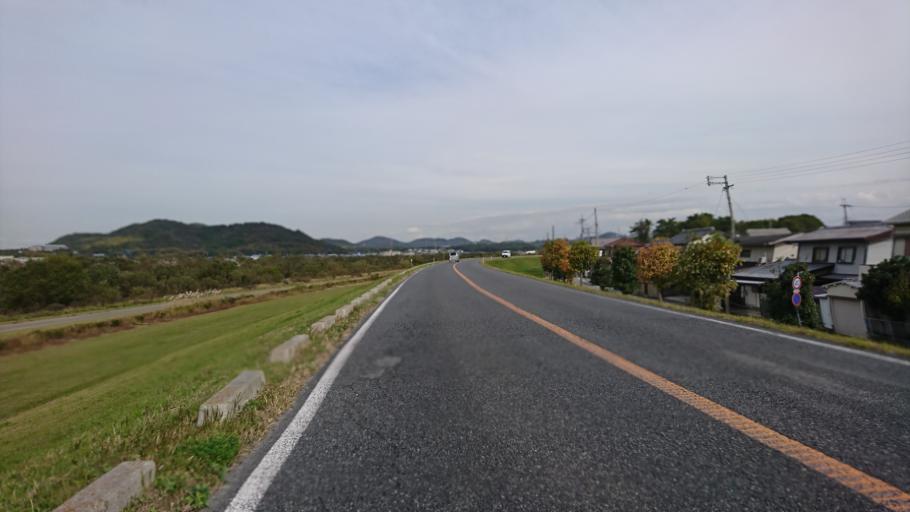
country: JP
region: Hyogo
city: Kakogawacho-honmachi
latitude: 34.7918
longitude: 134.8711
